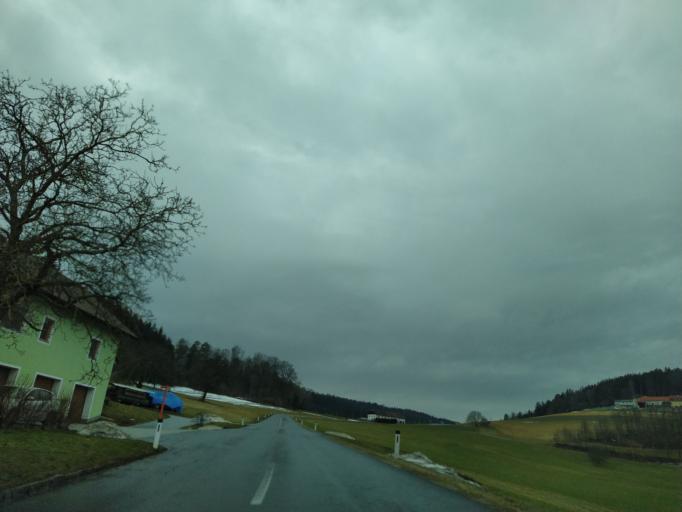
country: AT
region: Upper Austria
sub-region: Politischer Bezirk Urfahr-Umgebung
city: Kirchschlag bei Linz
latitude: 48.3960
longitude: 14.2835
